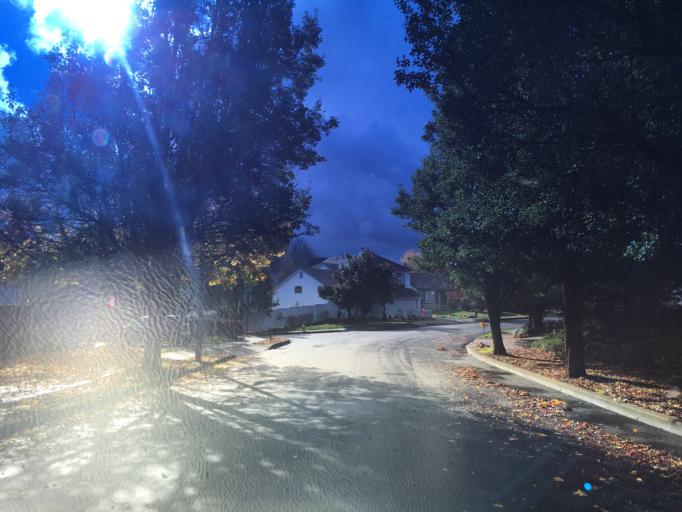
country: US
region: Oregon
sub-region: Multnomah County
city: Troutdale
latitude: 45.5115
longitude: -122.3826
